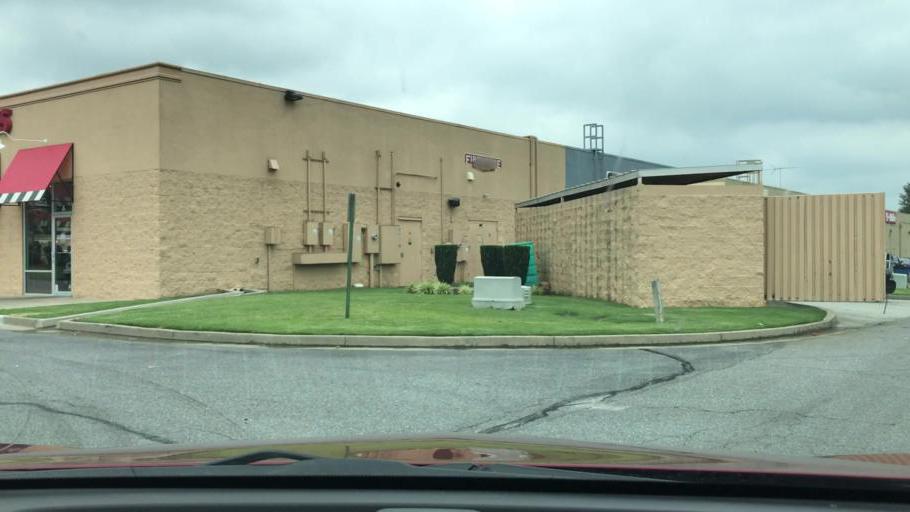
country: US
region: Georgia
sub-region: Forsyth County
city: Cumming
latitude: 34.1812
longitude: -84.1326
